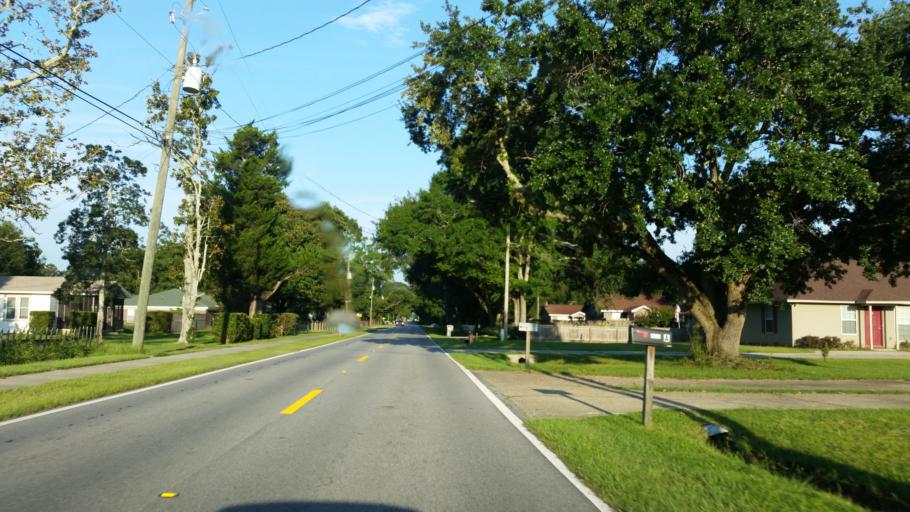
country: US
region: Florida
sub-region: Escambia County
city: Bellview
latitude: 30.4687
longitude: -87.3090
